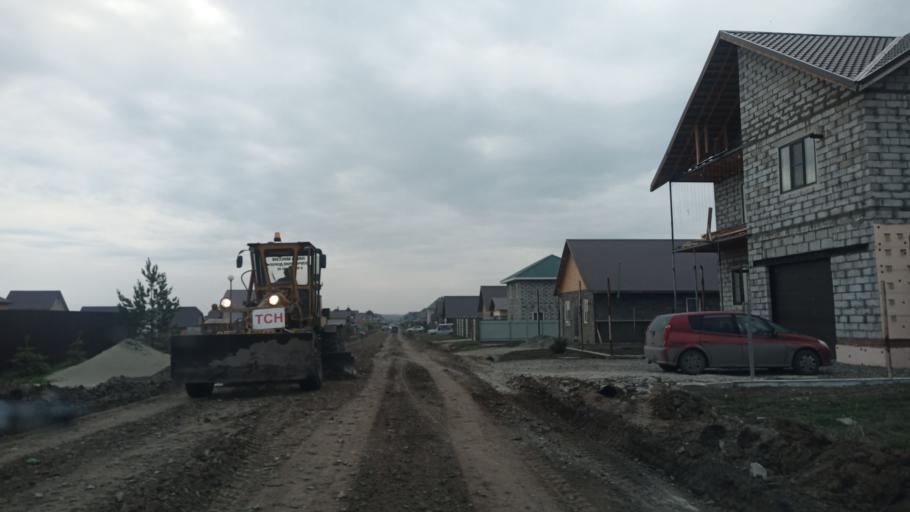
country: RU
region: Altai Krai
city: Yuzhnyy
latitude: 53.2273
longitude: 83.6911
